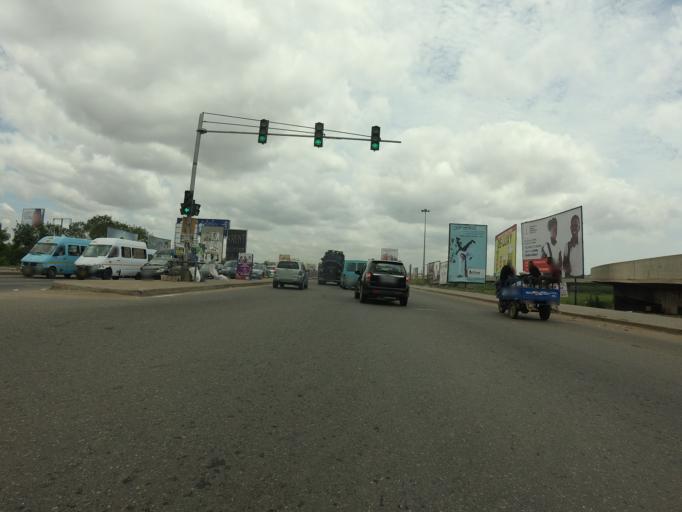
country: GH
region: Greater Accra
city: Gbawe
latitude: 5.5712
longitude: -0.2831
